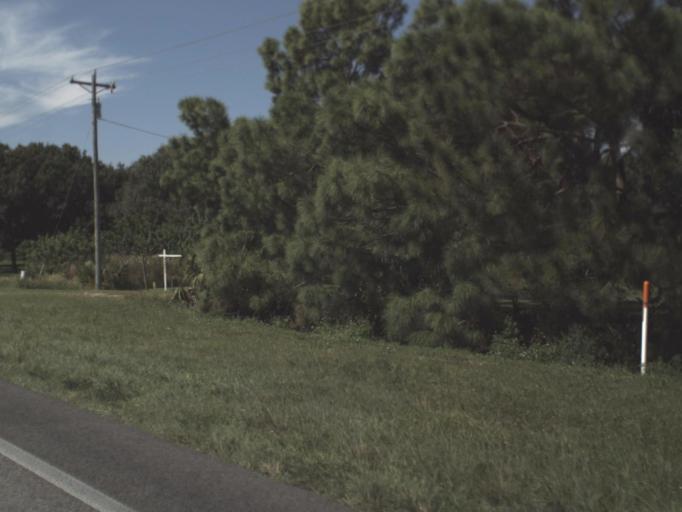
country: US
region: Florida
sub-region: Hendry County
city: Harlem
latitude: 26.7544
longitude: -80.9845
